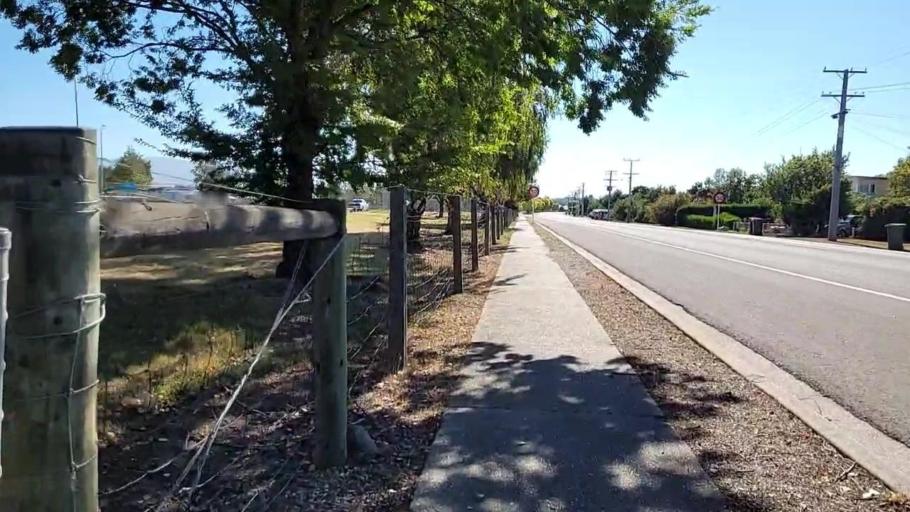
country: NZ
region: Otago
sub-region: Queenstown-Lakes District
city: Wanaka
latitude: -45.1011
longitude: 169.5963
